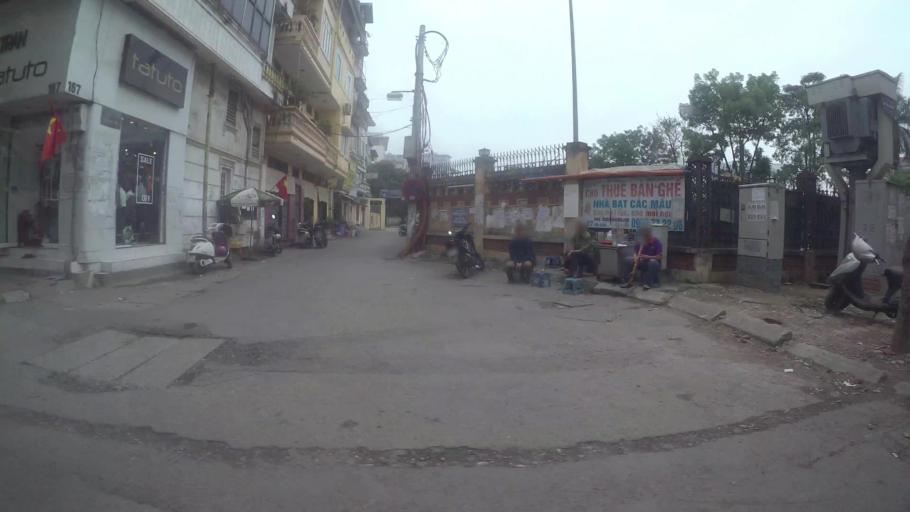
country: VN
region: Ha Noi
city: Dong Da
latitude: 21.0349
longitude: 105.8254
